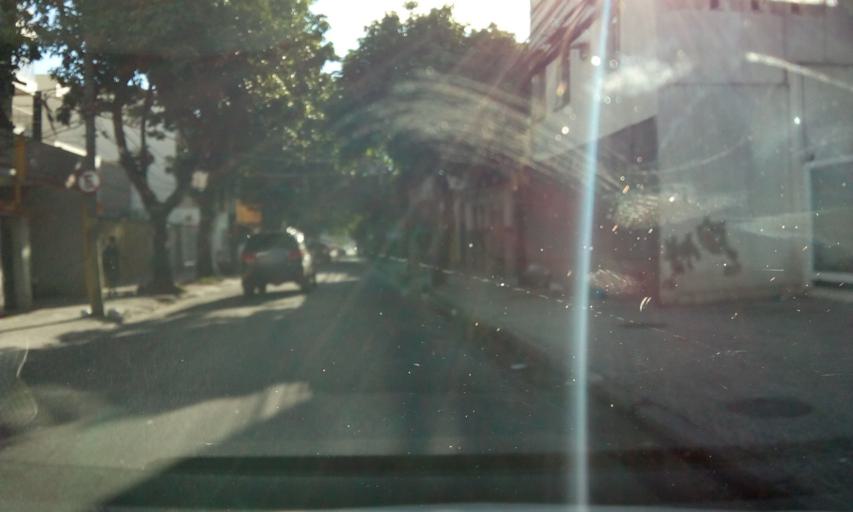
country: BR
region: Rio de Janeiro
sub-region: Rio De Janeiro
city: Rio de Janeiro
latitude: -22.9583
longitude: -43.1938
